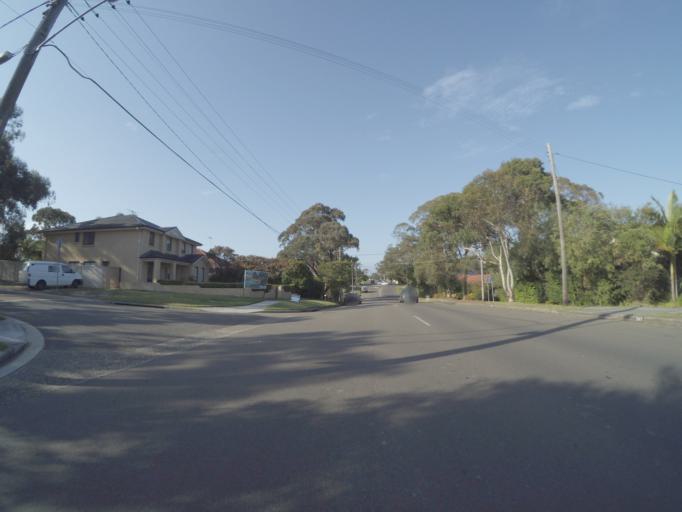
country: AU
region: New South Wales
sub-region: Sutherland Shire
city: Caringbah
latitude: -34.0484
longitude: 151.1170
